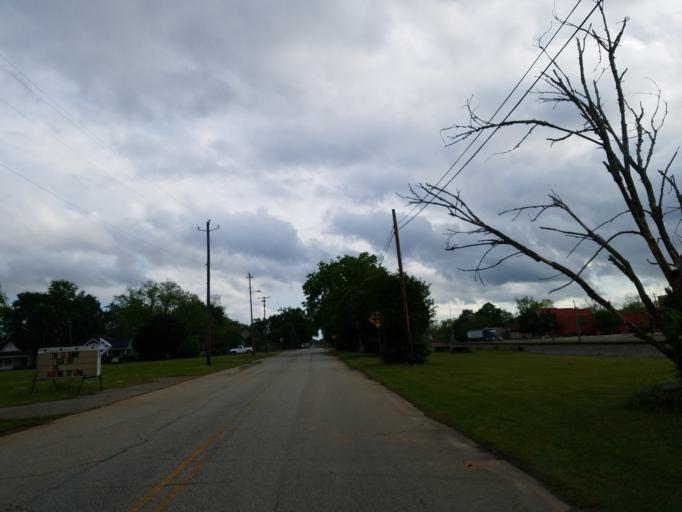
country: US
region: Georgia
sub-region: Dooly County
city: Unadilla
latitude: 32.2622
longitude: -83.7347
